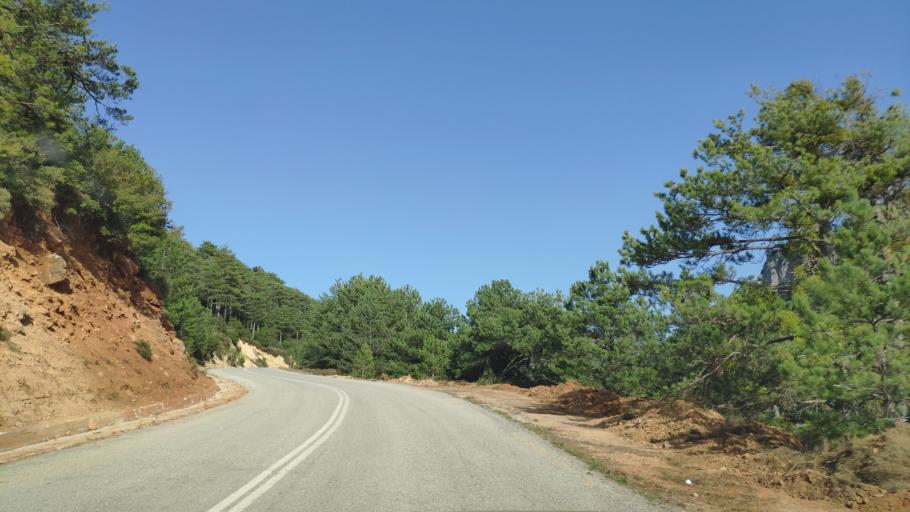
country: GR
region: West Greece
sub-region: Nomos Achaias
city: Aiyira
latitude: 38.0003
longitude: 22.3864
